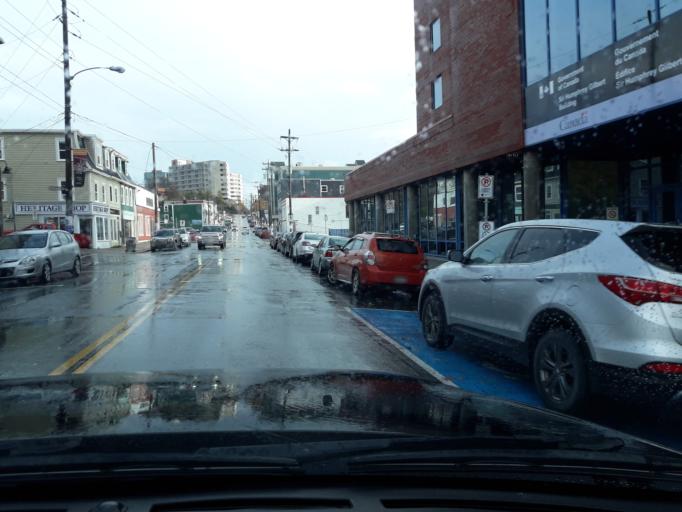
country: CA
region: Newfoundland and Labrador
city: St. John's
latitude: 47.5683
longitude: -52.7032
